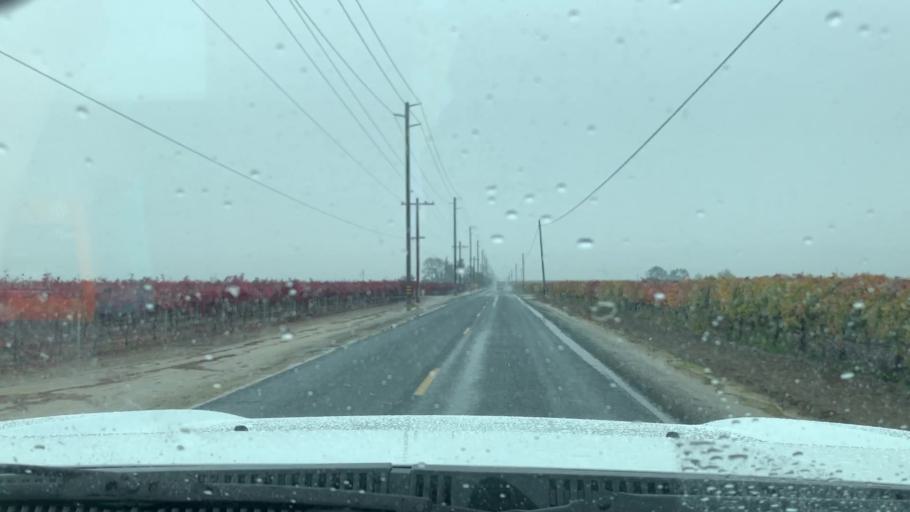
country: US
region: California
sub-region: Kern County
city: Delano
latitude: 35.8340
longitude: -119.2179
